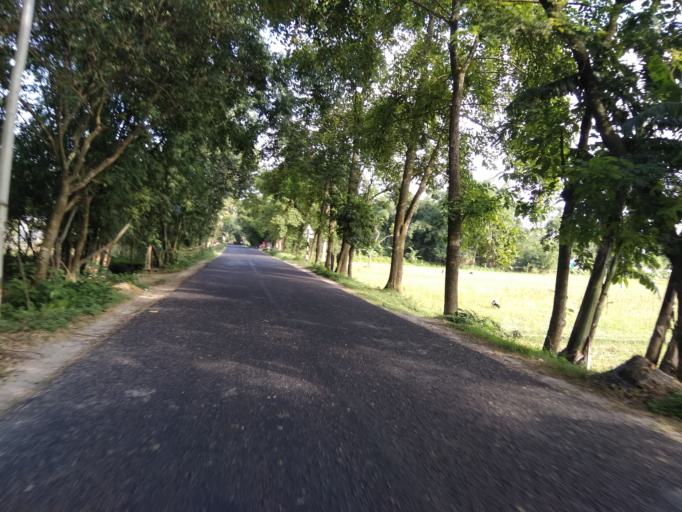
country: BD
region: Rangpur Division
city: Rangpur
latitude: 25.8339
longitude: 89.1164
